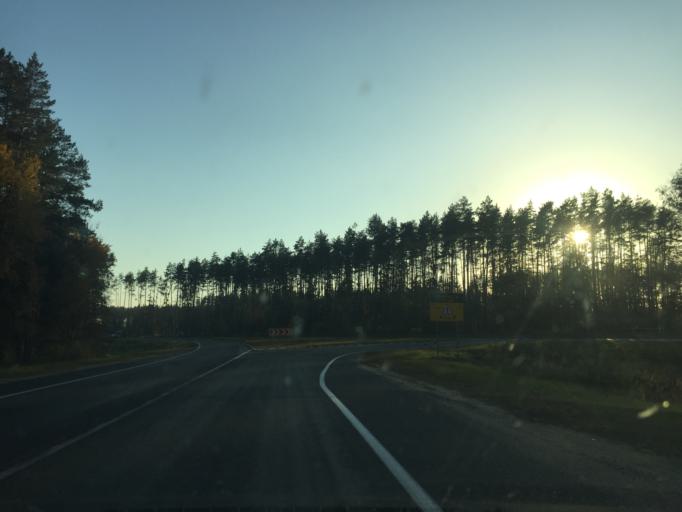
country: BY
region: Mogilev
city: Poselok Voskhod
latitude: 53.7673
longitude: 30.3657
